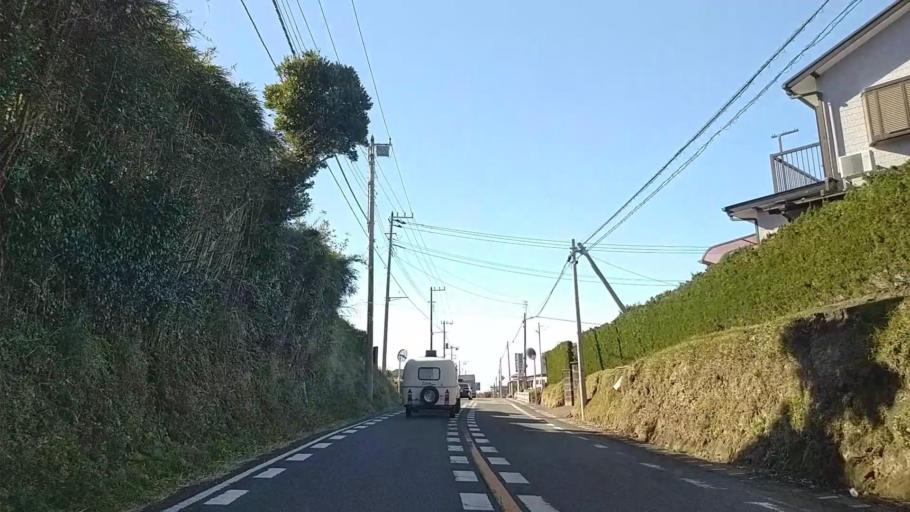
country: JP
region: Chiba
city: Tateyama
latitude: 34.9265
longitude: 139.8345
